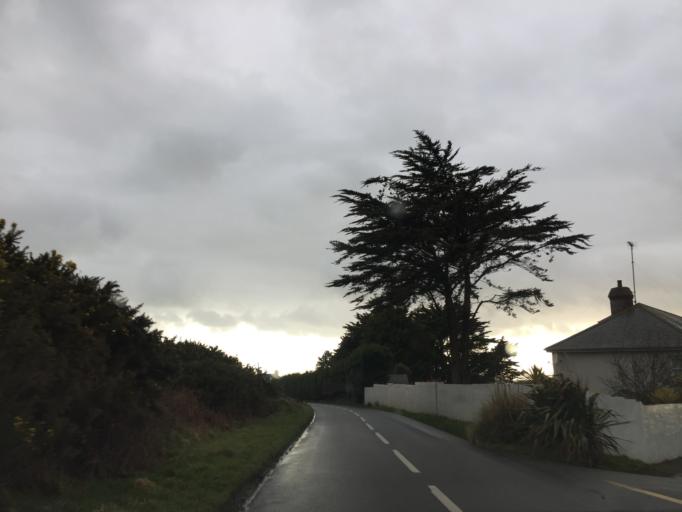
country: JE
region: St Helier
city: Saint Helier
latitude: 49.2343
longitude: -2.2309
